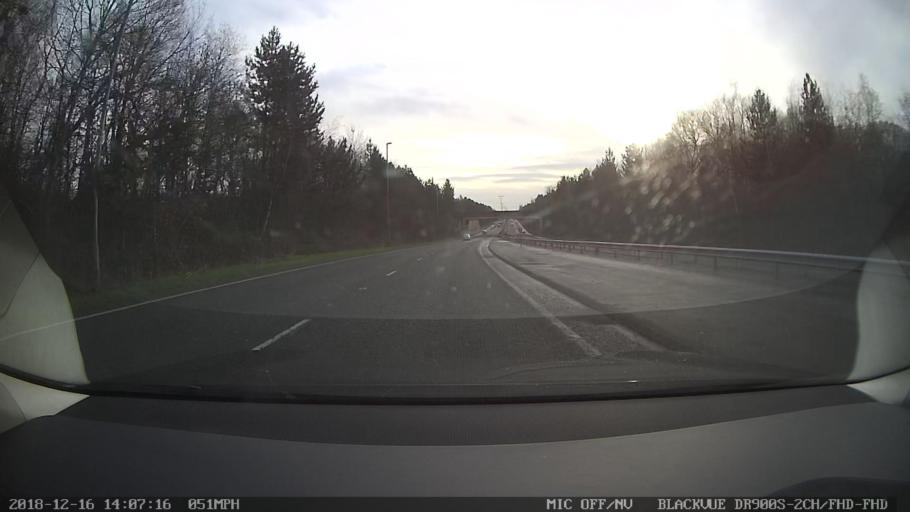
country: GB
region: England
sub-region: Borough of Stockport
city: Cheadle Hulme
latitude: 53.3744
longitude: -2.2113
